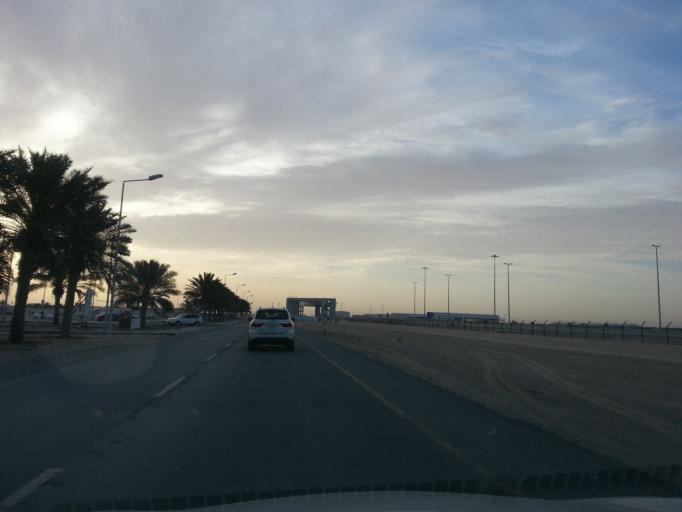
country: AE
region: Abu Dhabi
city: Abu Dhabi
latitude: 24.7810
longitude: 54.7267
